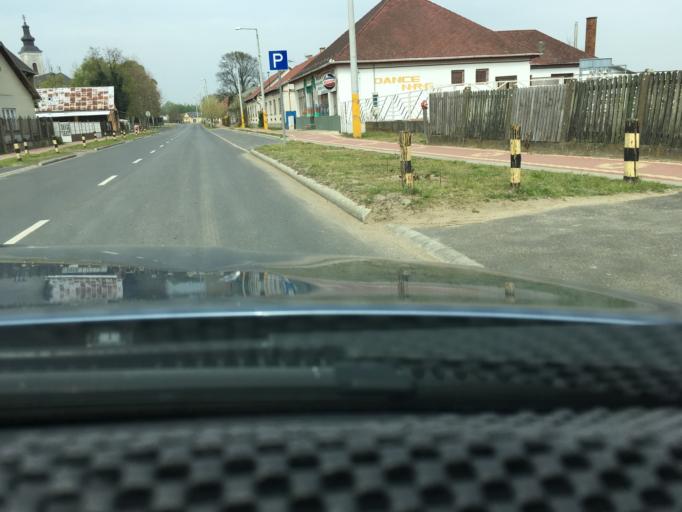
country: HU
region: Szabolcs-Szatmar-Bereg
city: Nyirlugos
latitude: 47.6929
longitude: 22.0421
